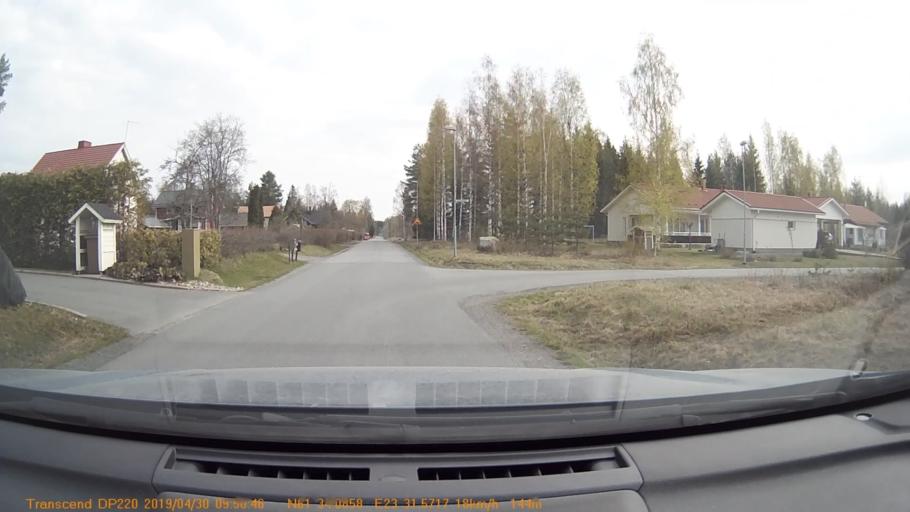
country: FI
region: Pirkanmaa
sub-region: Tampere
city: Yloejaervi
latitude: 61.5680
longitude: 23.5263
